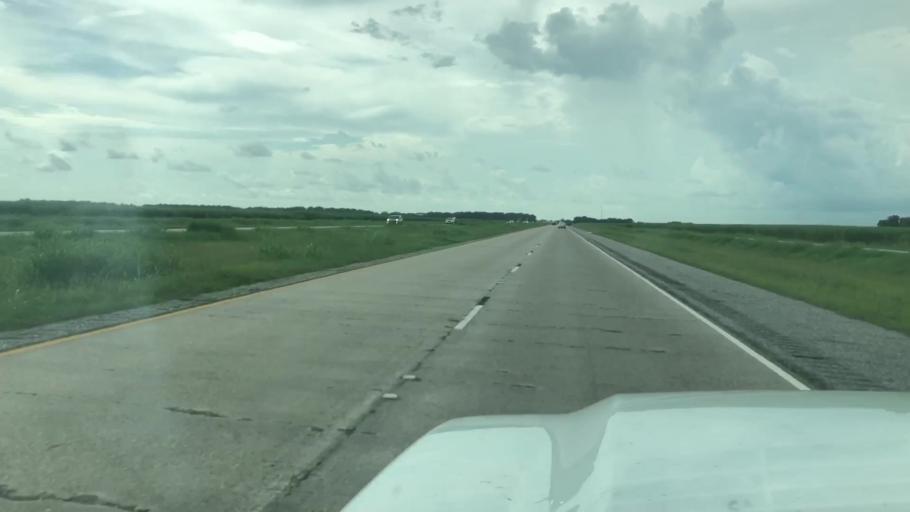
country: US
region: Louisiana
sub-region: Saint Mary Parish
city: Baldwin
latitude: 29.8478
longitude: -91.5908
